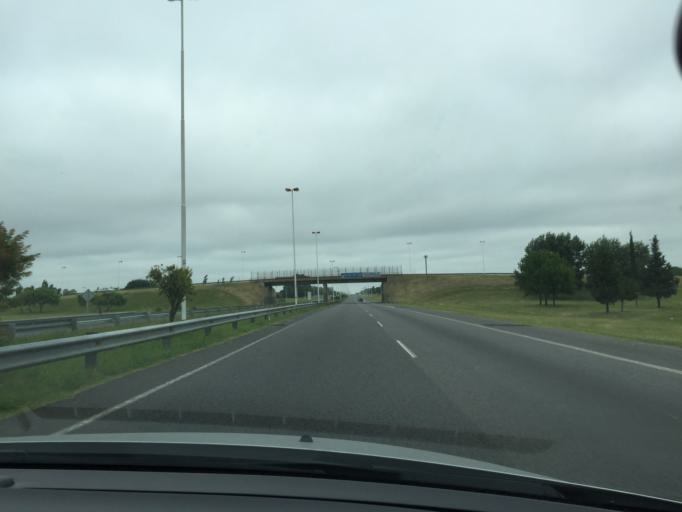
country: AR
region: Buenos Aires
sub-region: Partido de Ezeiza
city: Ezeiza
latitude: -34.8746
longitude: -58.5849
